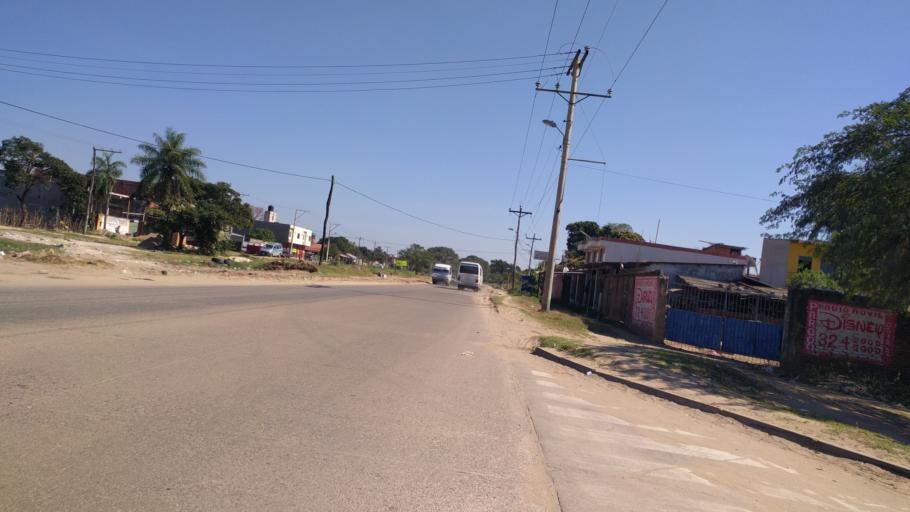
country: BO
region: Santa Cruz
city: Santa Cruz de la Sierra
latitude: -17.8417
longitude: -63.2166
